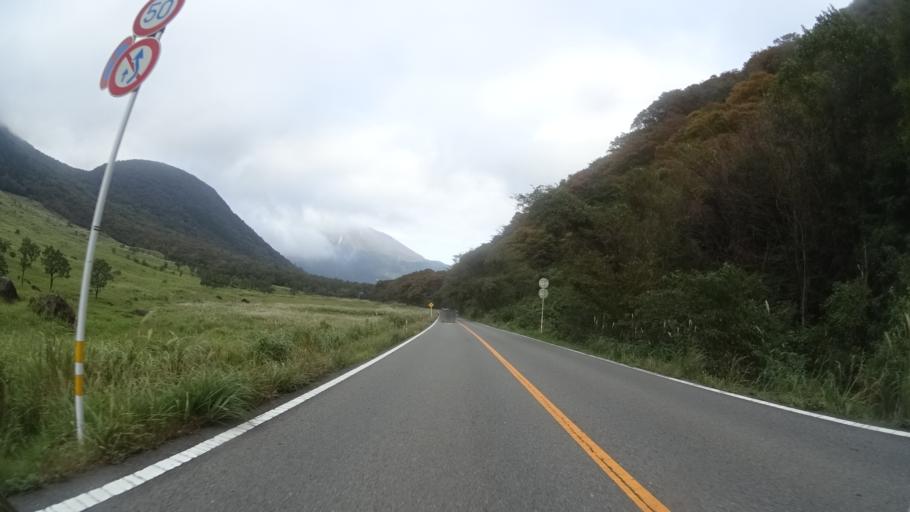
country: JP
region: Oita
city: Beppu
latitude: 33.2657
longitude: 131.3994
